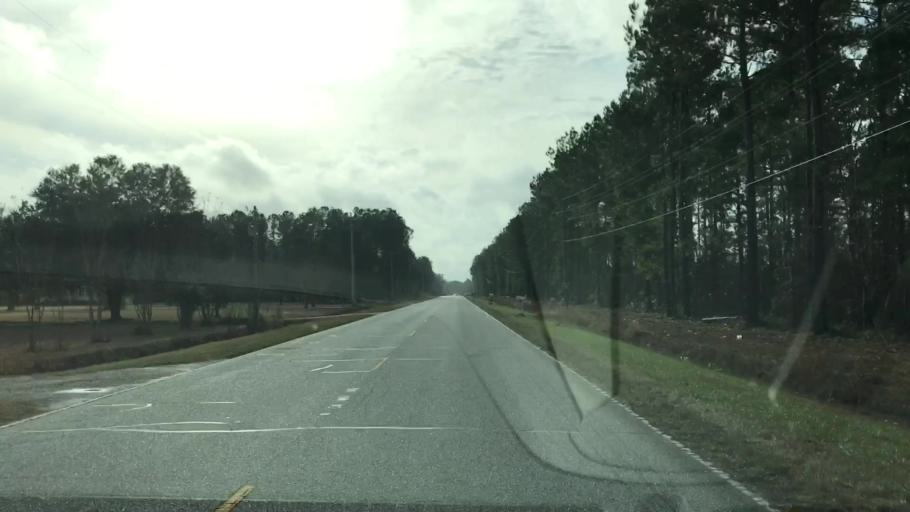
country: US
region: South Carolina
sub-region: Williamsburg County
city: Andrews
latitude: 33.3674
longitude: -79.6423
